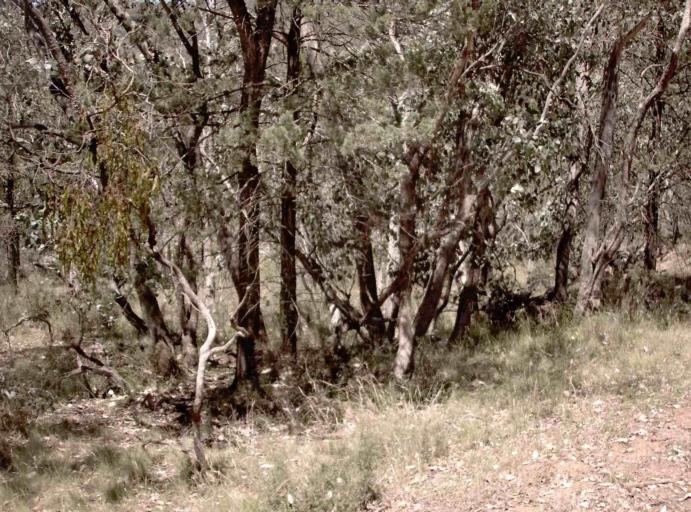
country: AU
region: New South Wales
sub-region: Snowy River
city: Jindabyne
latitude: -37.0899
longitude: 148.4355
